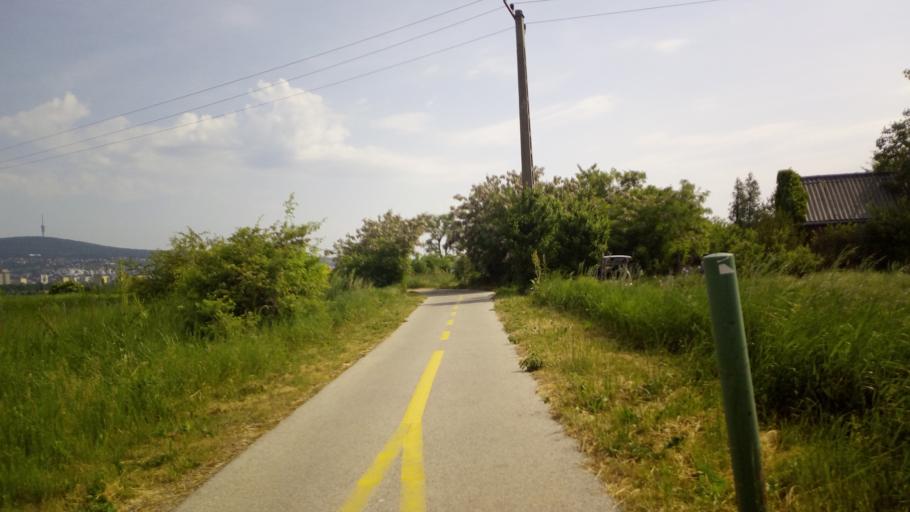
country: HU
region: Baranya
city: Pellerd
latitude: 46.0478
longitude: 18.1915
